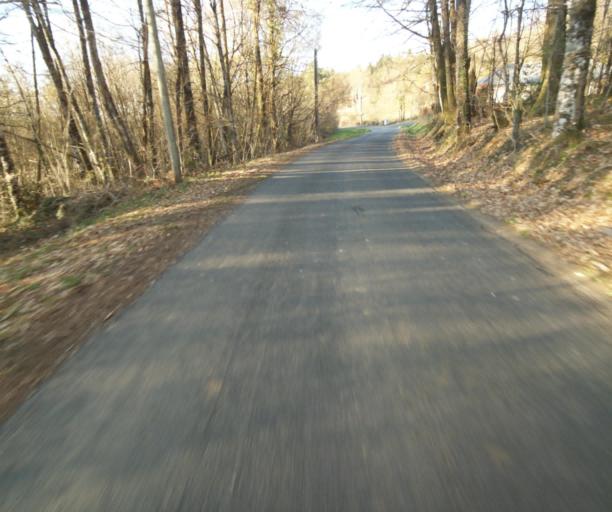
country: FR
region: Limousin
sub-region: Departement de la Correze
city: Seilhac
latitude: 45.3543
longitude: 1.7056
